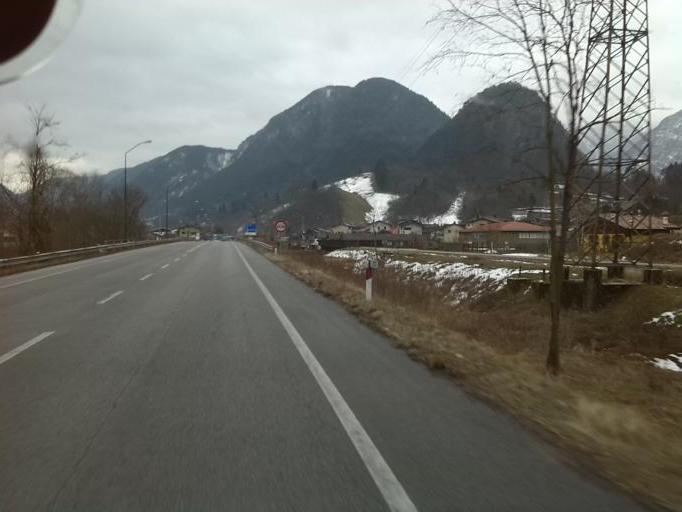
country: IT
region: Friuli Venezia Giulia
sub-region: Provincia di Udine
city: Resiutta
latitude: 46.3946
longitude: 13.2160
